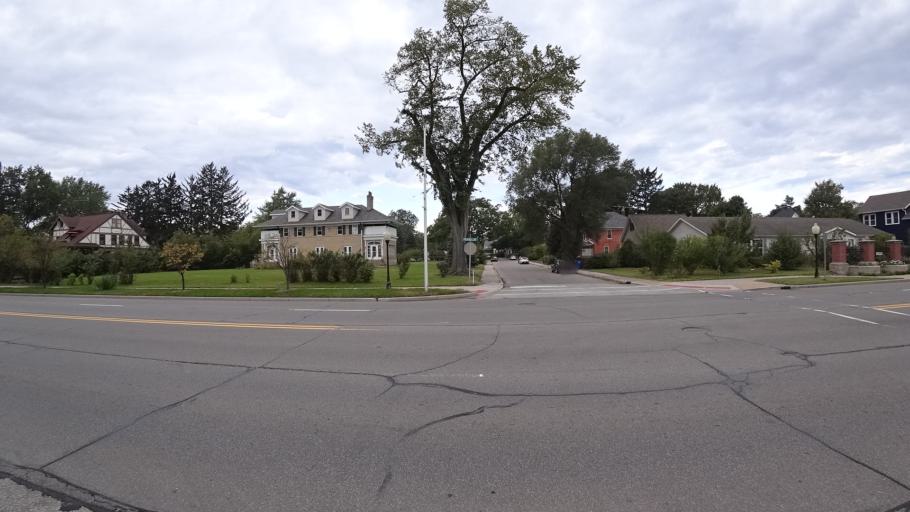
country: US
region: Indiana
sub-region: LaPorte County
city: Michigan City
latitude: 41.6980
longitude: -86.8941
